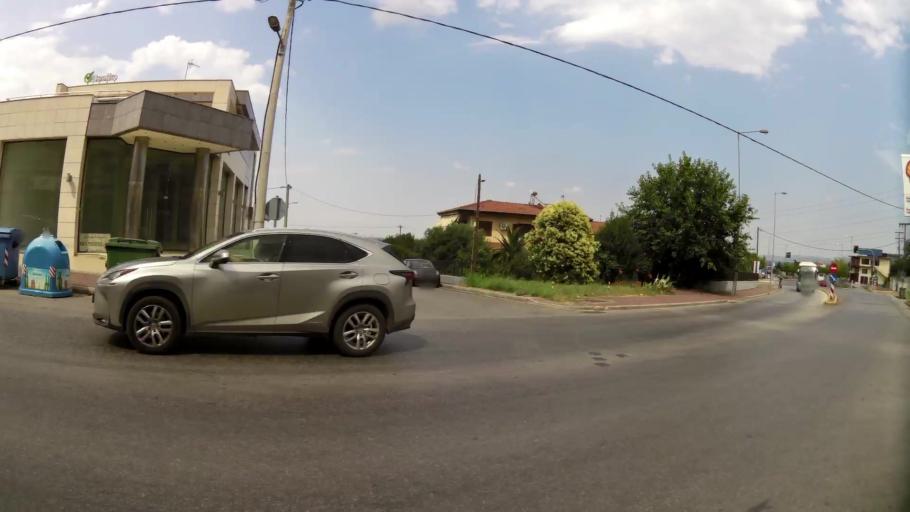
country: GR
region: Central Macedonia
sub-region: Nomos Imathias
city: Veroia
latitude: 40.5096
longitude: 22.2173
